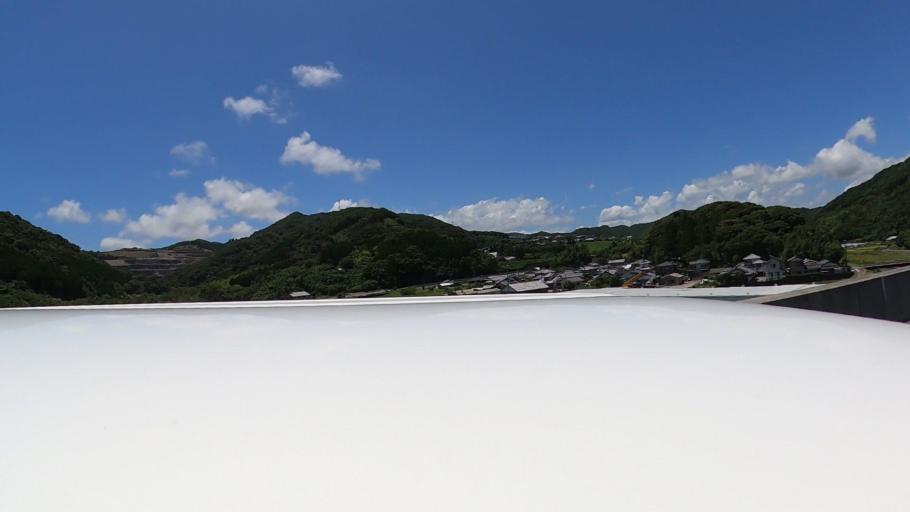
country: JP
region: Miyazaki
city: Nobeoka
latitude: 32.3982
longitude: 131.6183
